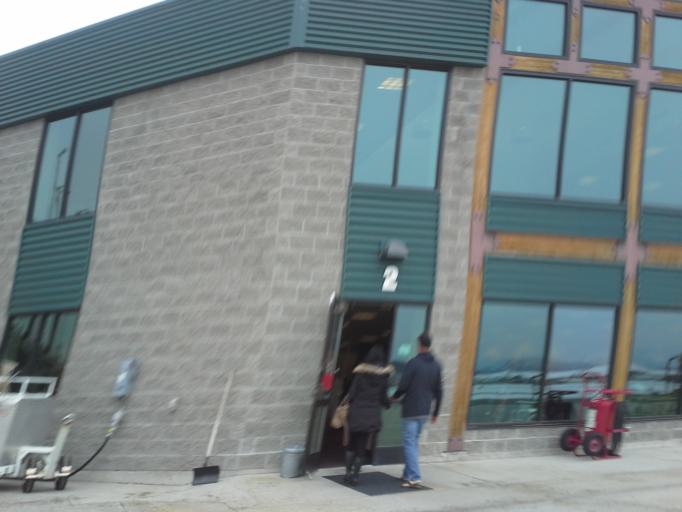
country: US
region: Montana
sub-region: Lewis and Clark County
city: Helena
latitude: 46.6099
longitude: -111.9901
